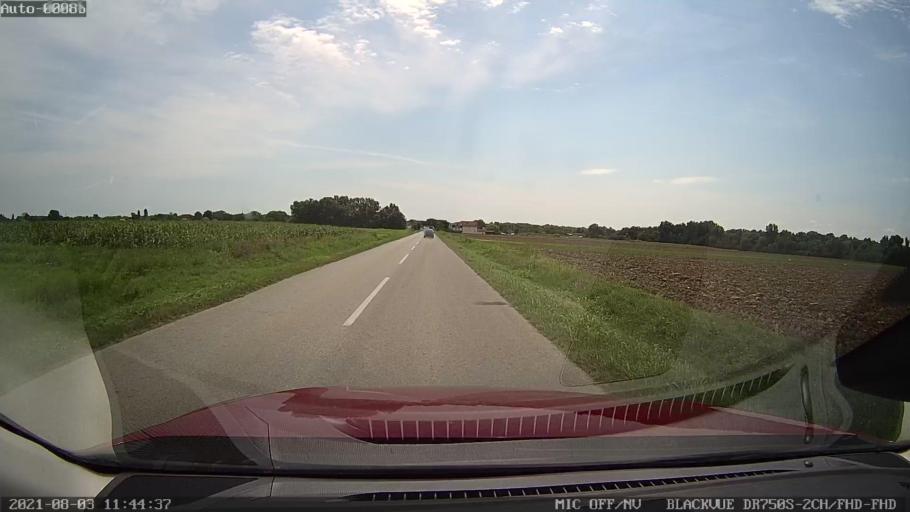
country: HR
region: Osjecko-Baranjska
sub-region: Grad Osijek
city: Bilje
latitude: 45.6020
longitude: 18.7742
